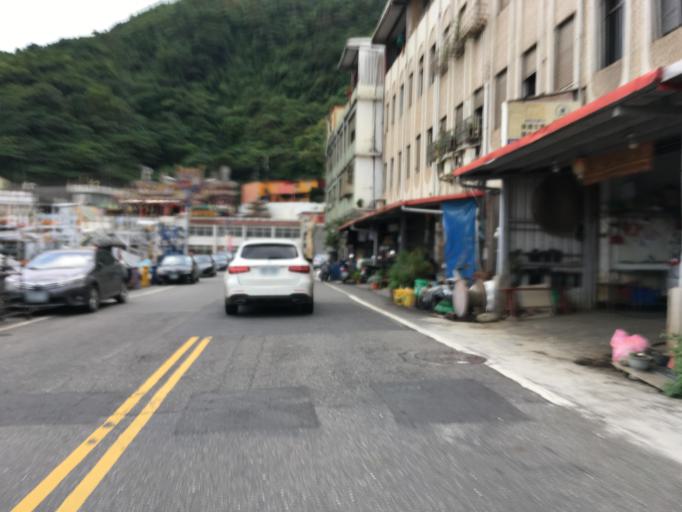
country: TW
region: Taiwan
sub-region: Yilan
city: Yilan
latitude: 24.5784
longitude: 121.8688
